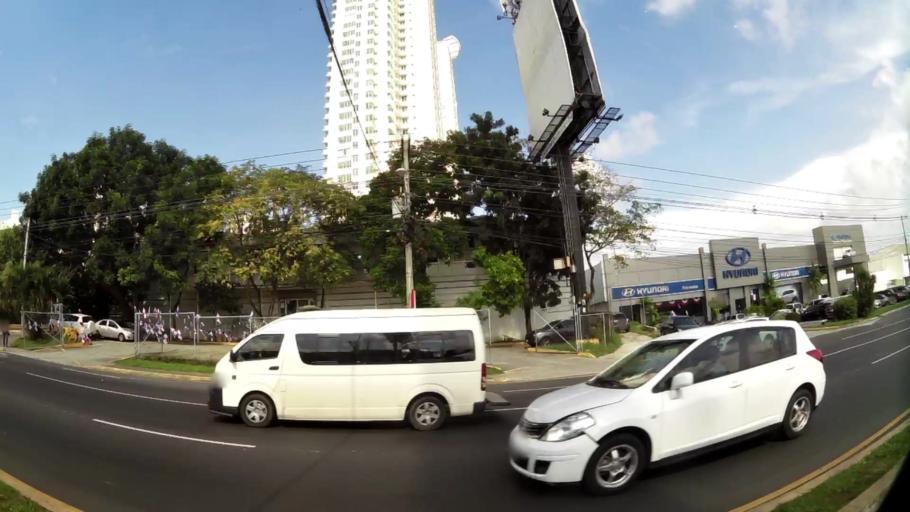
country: PA
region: Panama
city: Panama
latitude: 8.9945
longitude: -79.5291
